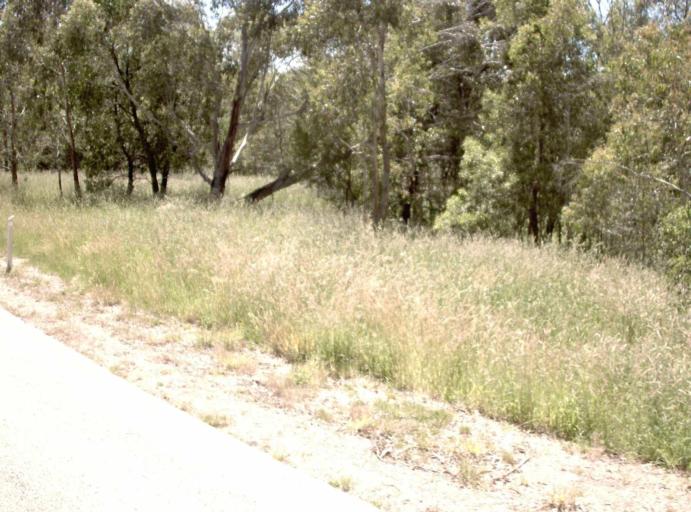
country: AU
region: Victoria
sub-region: East Gippsland
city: Lakes Entrance
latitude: -37.2125
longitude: 148.2686
